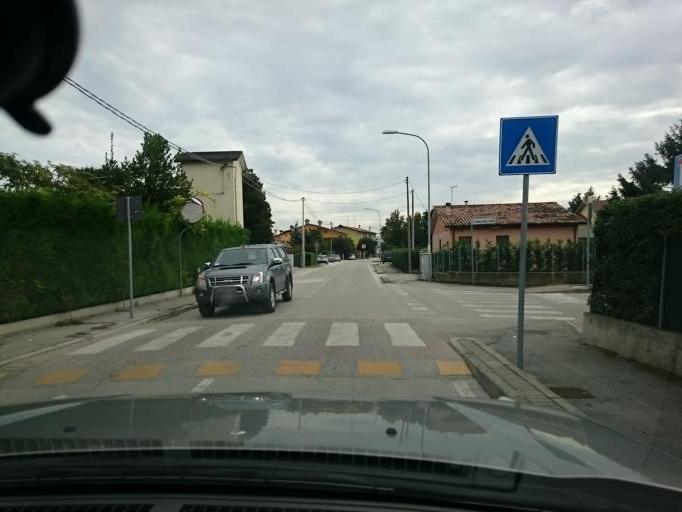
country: IT
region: Veneto
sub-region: Provincia di Padova
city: Arzergrande
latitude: 45.2849
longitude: 12.0589
